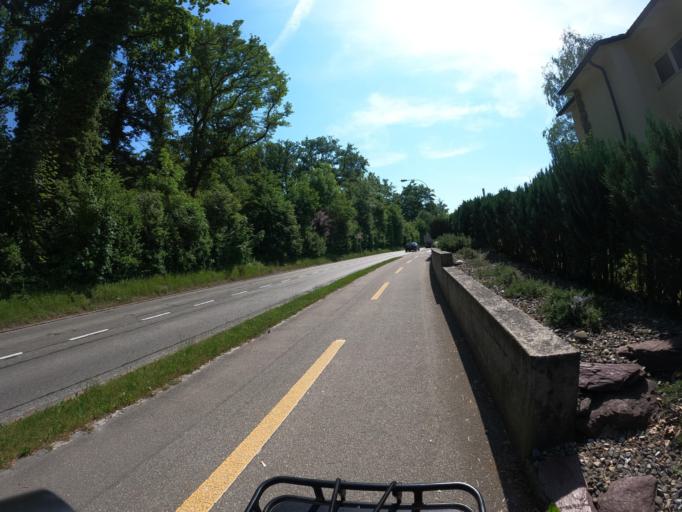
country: CH
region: Zurich
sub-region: Bezirk Buelach
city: Buelach / Niederflachs
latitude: 47.5219
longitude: 8.5296
